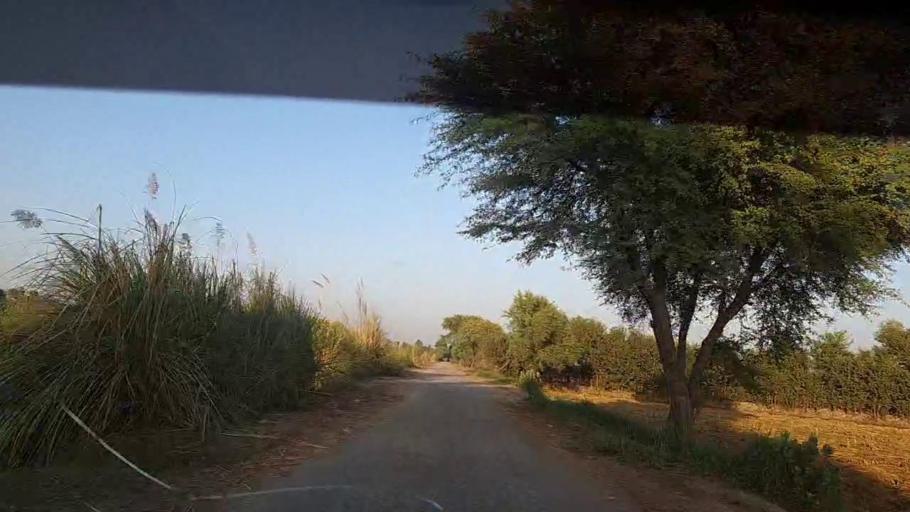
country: PK
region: Sindh
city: Ratodero
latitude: 27.8801
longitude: 68.2050
